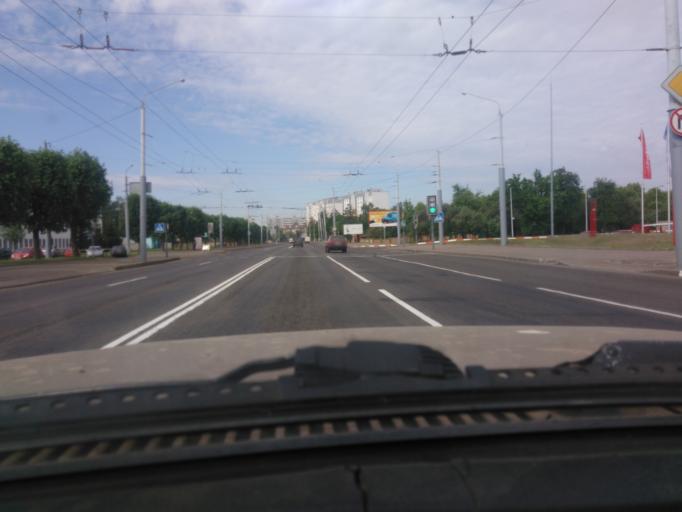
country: BY
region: Mogilev
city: Buynichy
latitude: 53.8884
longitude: 30.2824
